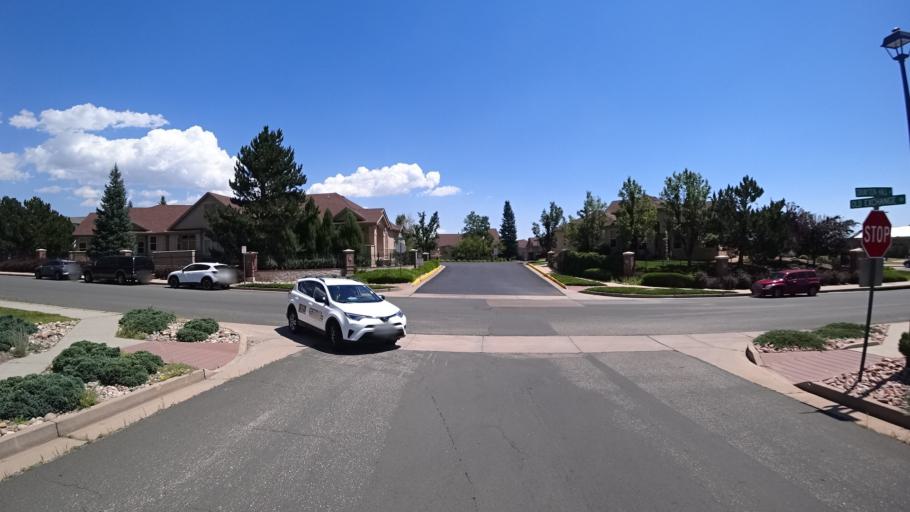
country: US
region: Colorado
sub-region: El Paso County
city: Black Forest
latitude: 38.9530
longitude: -104.7629
